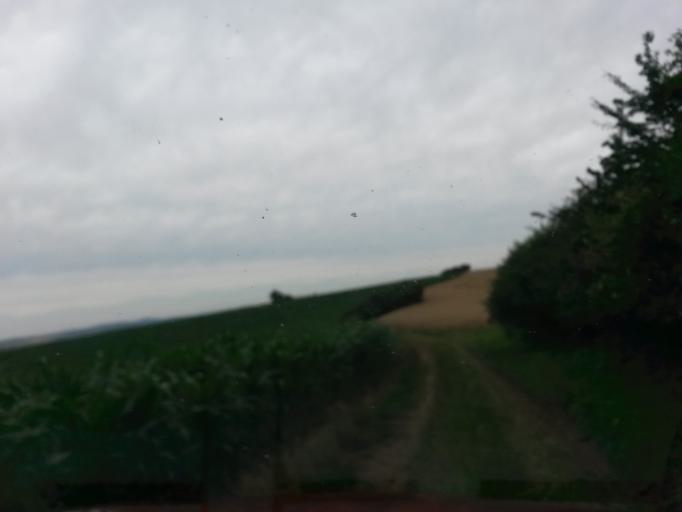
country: SK
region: Nitriansky
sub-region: Okres Nitra
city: Nitra
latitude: 48.3449
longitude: 17.9850
